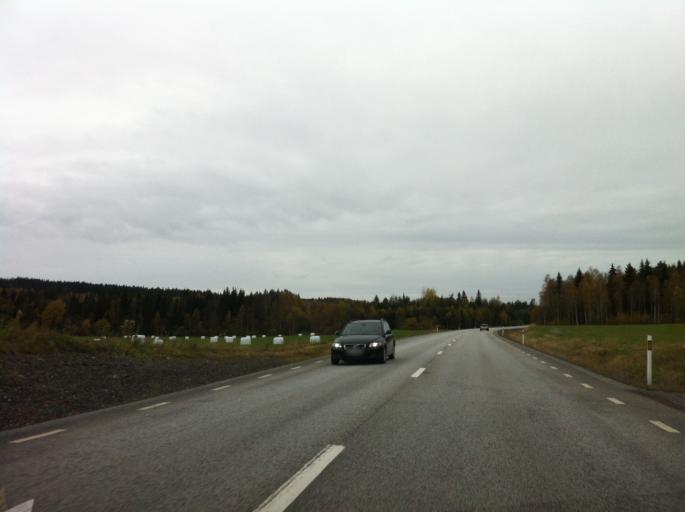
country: SE
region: OErebro
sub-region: Ljusnarsbergs Kommun
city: Kopparberg
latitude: 59.8445
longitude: 15.0749
